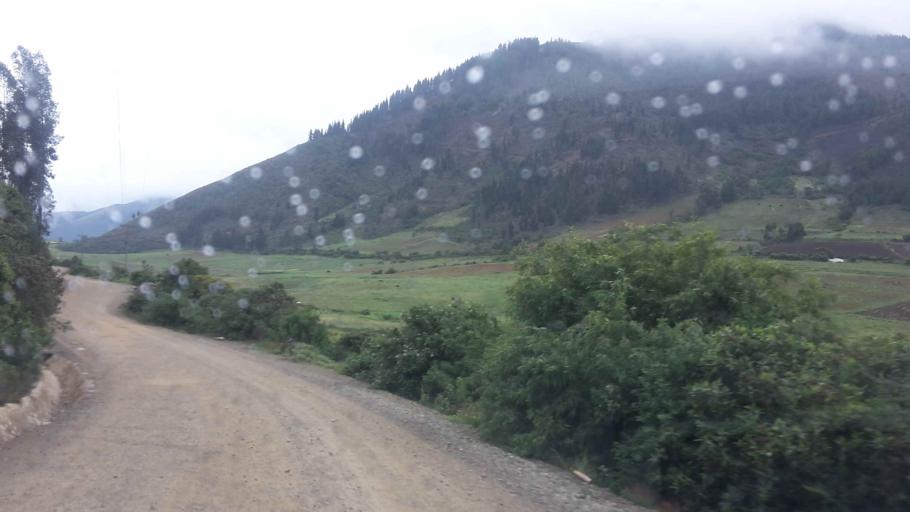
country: BO
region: Cochabamba
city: Totora
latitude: -17.5840
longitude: -65.2912
